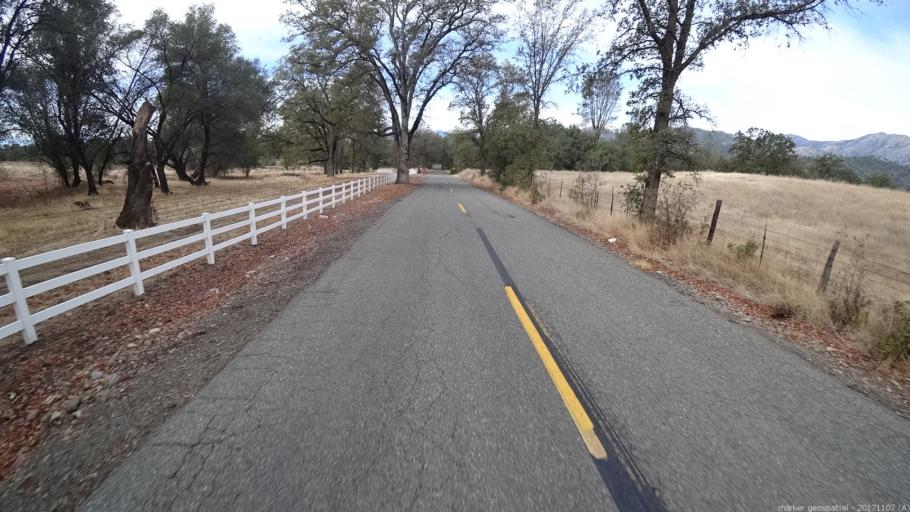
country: US
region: California
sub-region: Shasta County
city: Shasta
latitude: 40.5011
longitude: -122.5643
